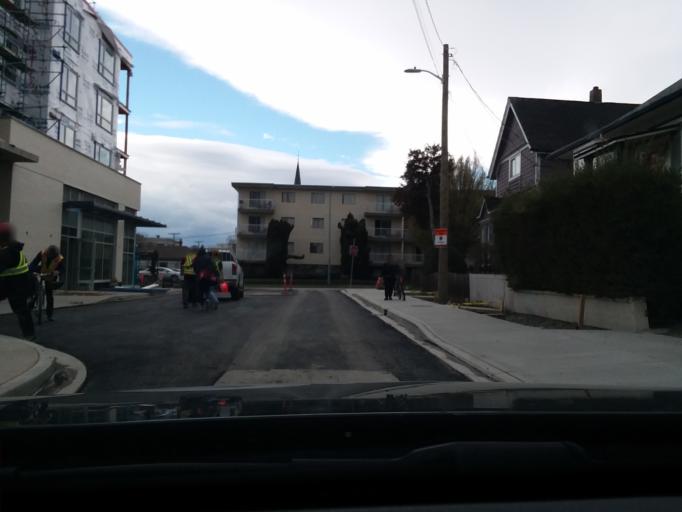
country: CA
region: British Columbia
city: Victoria
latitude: 48.4283
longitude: -123.3554
